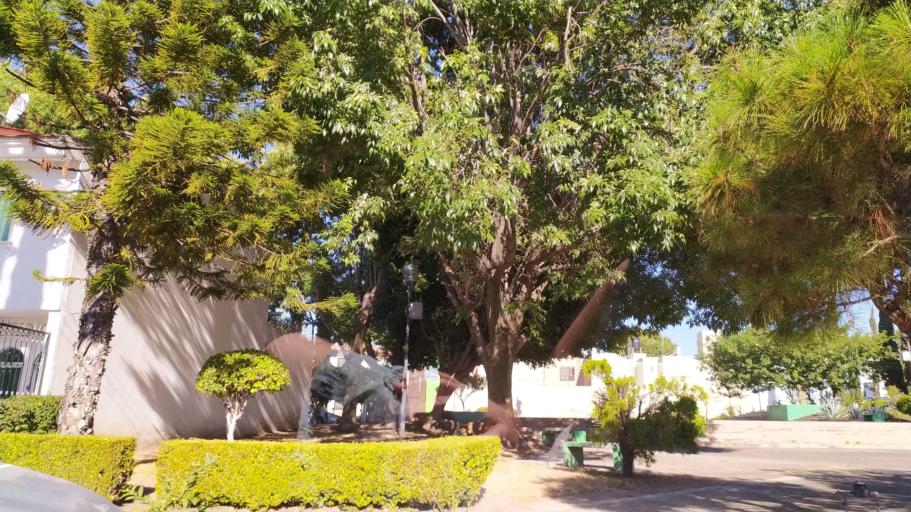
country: MX
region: Jalisco
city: Guadalajara
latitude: 20.6591
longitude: -103.4269
